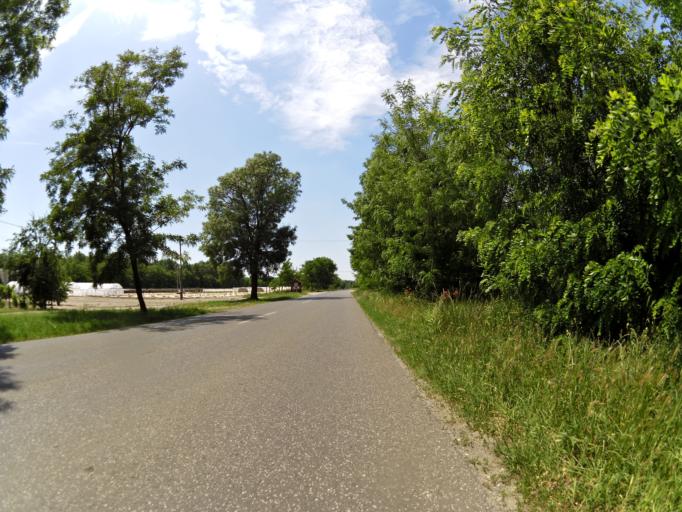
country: HU
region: Csongrad
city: Kistelek
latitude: 46.4878
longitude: 20.0249
